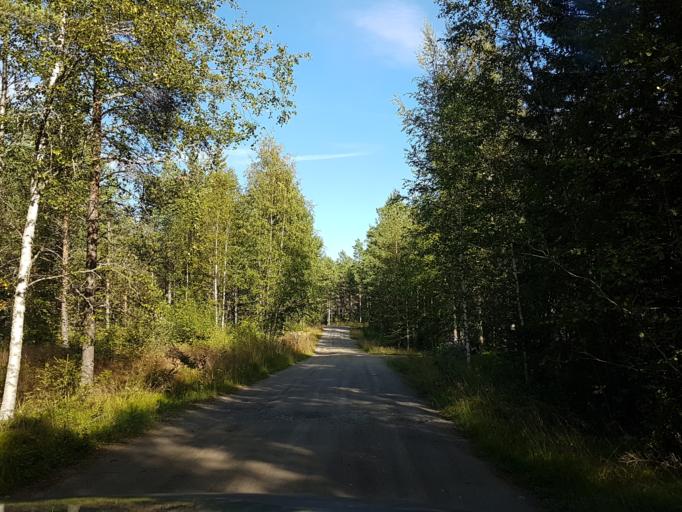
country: SE
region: Vaesterbotten
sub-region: Robertsfors Kommun
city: Robertsfors
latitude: 64.0452
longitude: 20.9044
